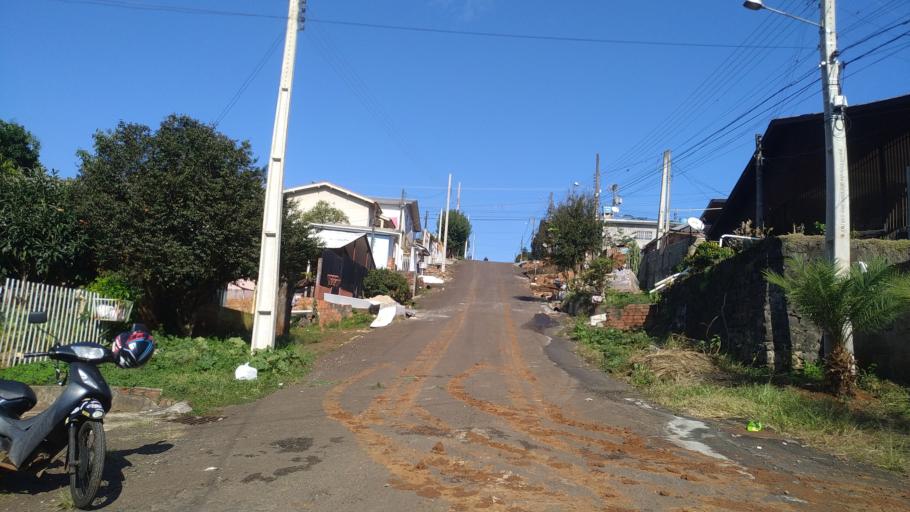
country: BR
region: Santa Catarina
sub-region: Chapeco
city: Chapeco
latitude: -27.1012
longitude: -52.6364
